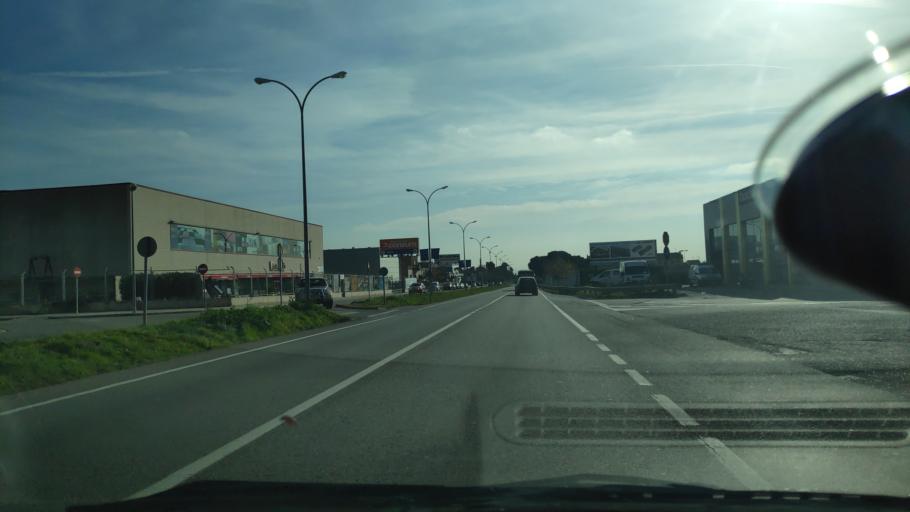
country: ES
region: Catalonia
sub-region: Provincia de Barcelona
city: Castellar del Valles
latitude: 41.6070
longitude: 2.0846
